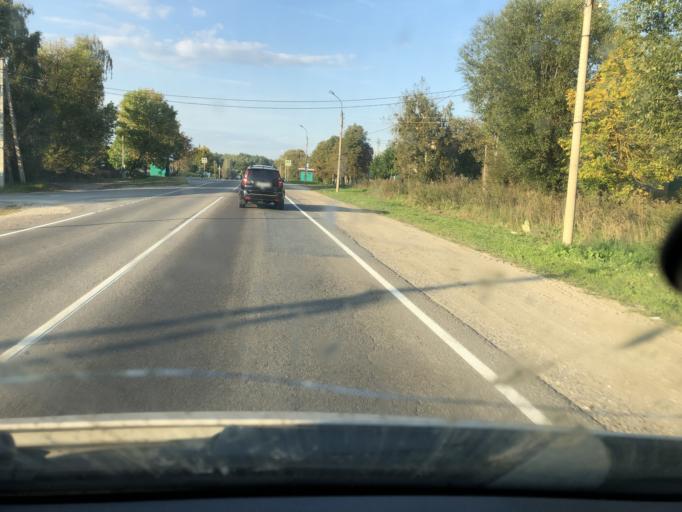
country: RU
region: Kaluga
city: Peremyshl'
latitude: 54.3803
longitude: 36.1994
